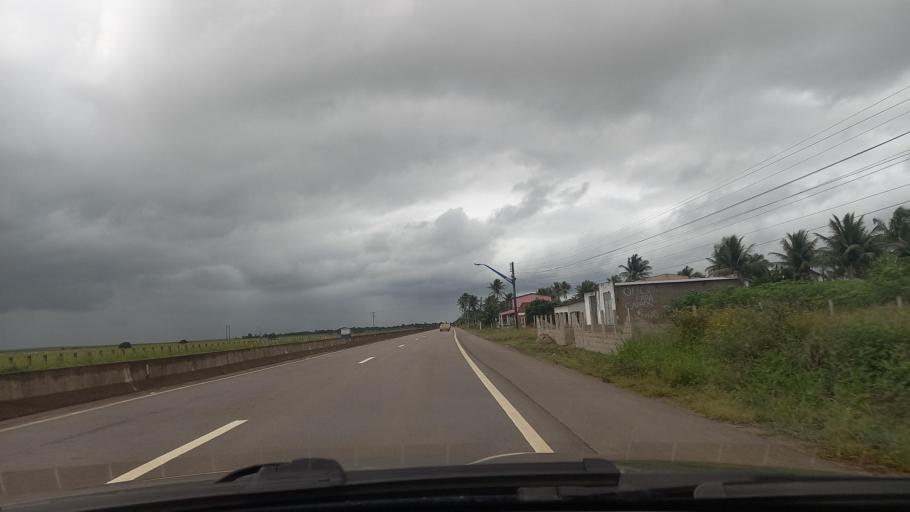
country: BR
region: Alagoas
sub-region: Limoeiro De Anadia
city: Cajueiro
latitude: -9.7438
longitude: -36.4657
